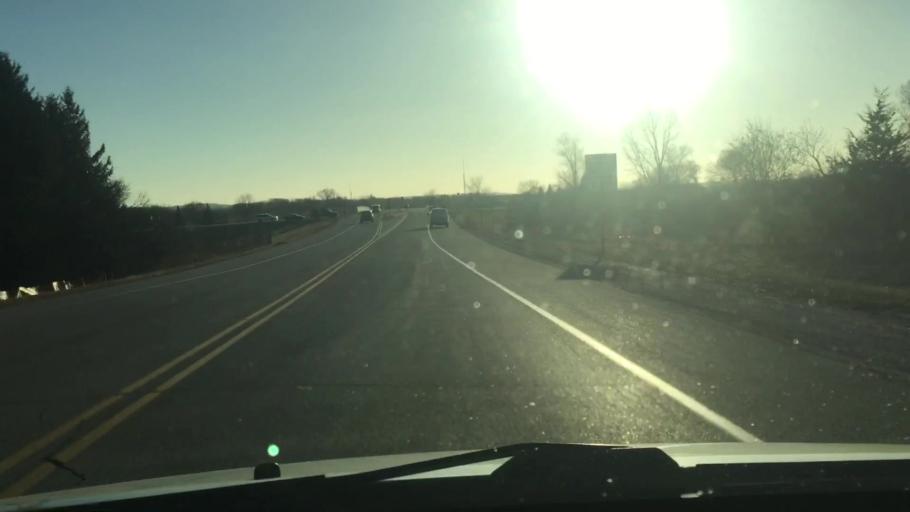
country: US
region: Wisconsin
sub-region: Waukesha County
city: Pewaukee
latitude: 43.0973
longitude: -88.2704
